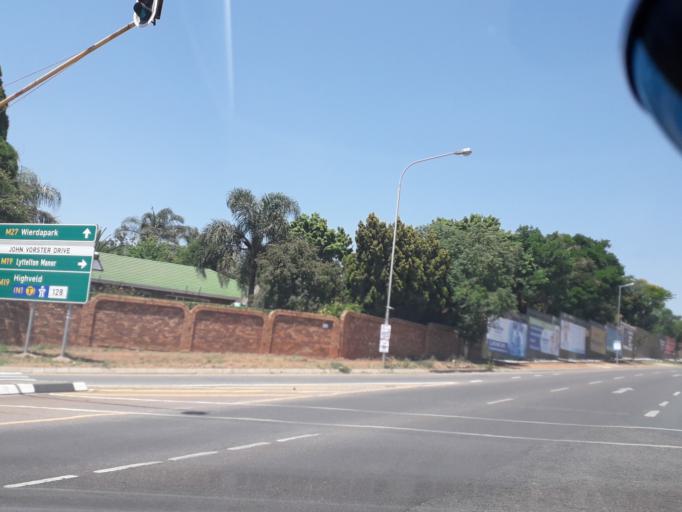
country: ZA
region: Gauteng
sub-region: City of Tshwane Metropolitan Municipality
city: Centurion
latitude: -25.8633
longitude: 28.1867
